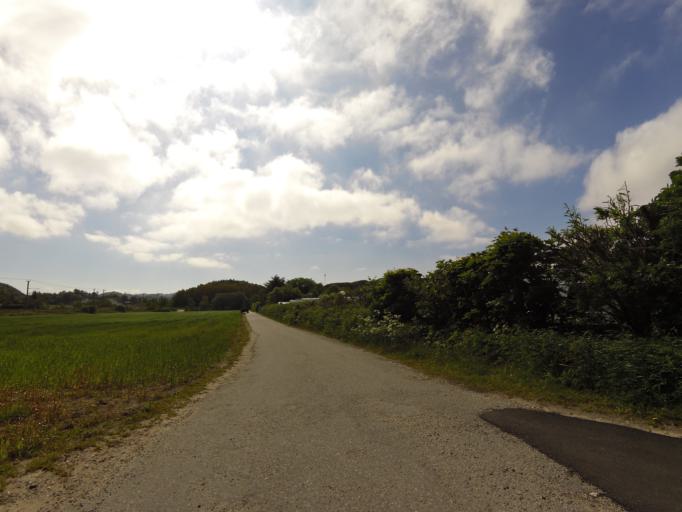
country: NO
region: Rogaland
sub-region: Ha
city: Vigrestad
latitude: 58.5219
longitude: 5.7967
